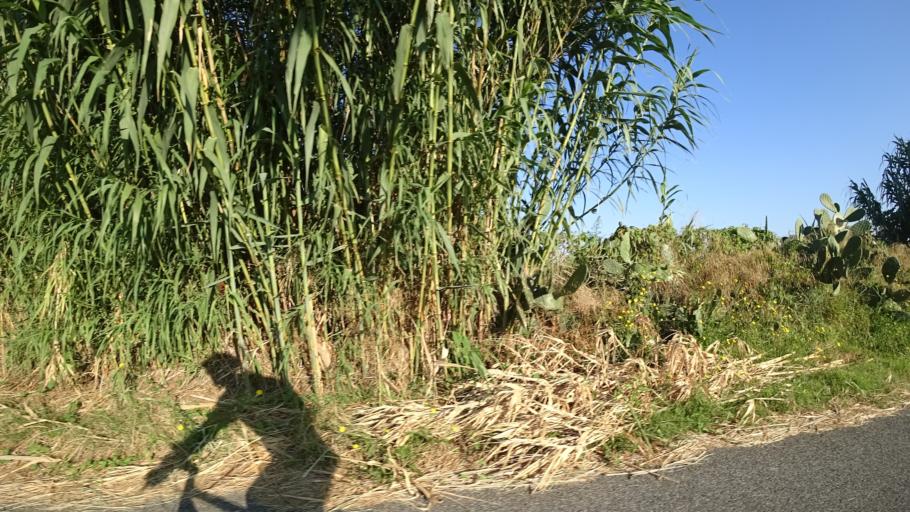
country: FR
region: Languedoc-Roussillon
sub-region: Departement des Pyrenees-Orientales
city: Sainte-Marie-Plage
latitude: 42.7177
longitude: 3.0285
